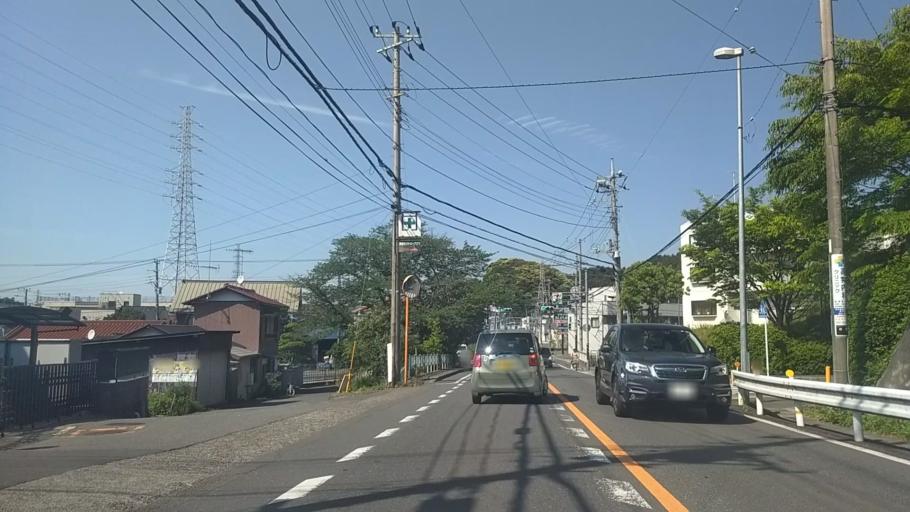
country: JP
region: Kanagawa
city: Kamakura
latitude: 35.3531
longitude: 139.5433
